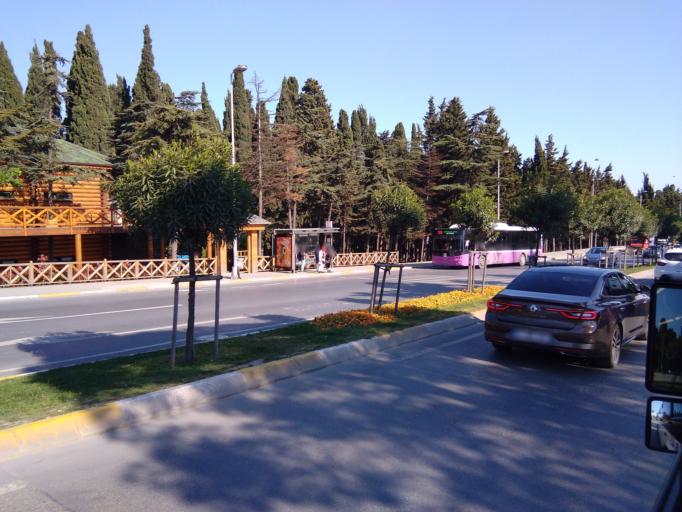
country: TR
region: Istanbul
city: Mahmutbey
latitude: 41.0328
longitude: 28.7894
